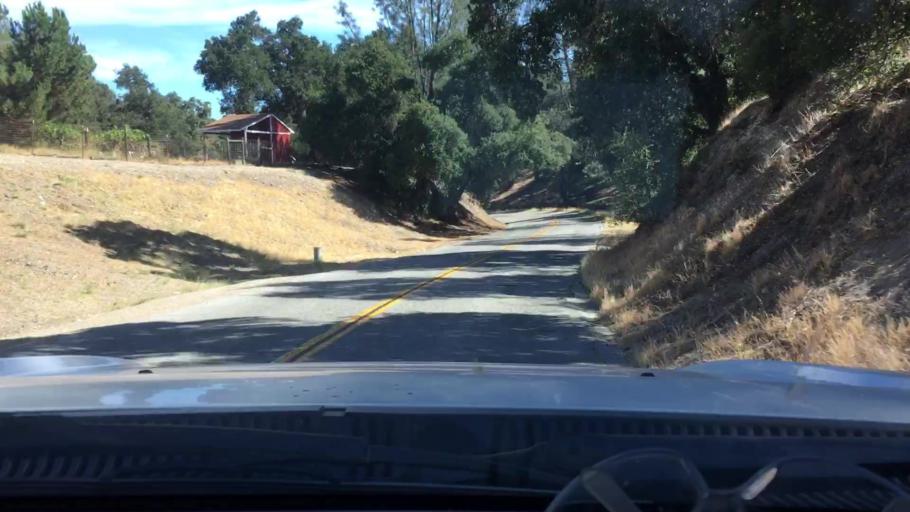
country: US
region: California
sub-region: San Luis Obispo County
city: Atascadero
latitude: 35.4530
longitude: -120.6541
